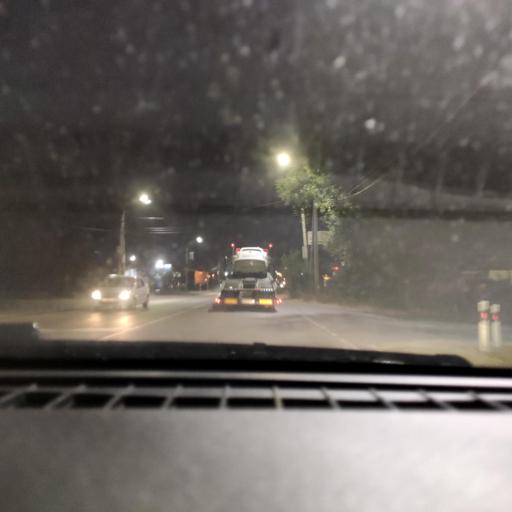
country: RU
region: Voronezj
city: Maslovka
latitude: 51.6408
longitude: 39.2940
